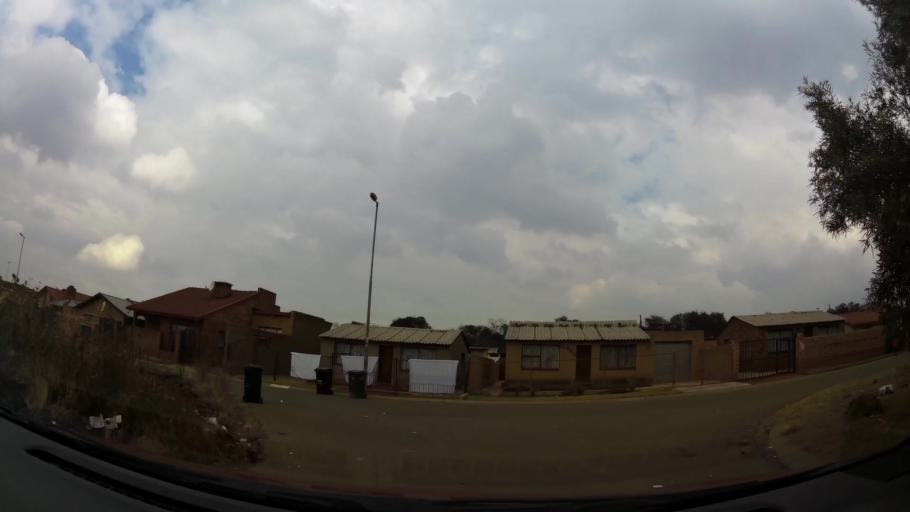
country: ZA
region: Gauteng
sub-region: City of Johannesburg Metropolitan Municipality
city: Soweto
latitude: -26.2604
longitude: 27.8311
